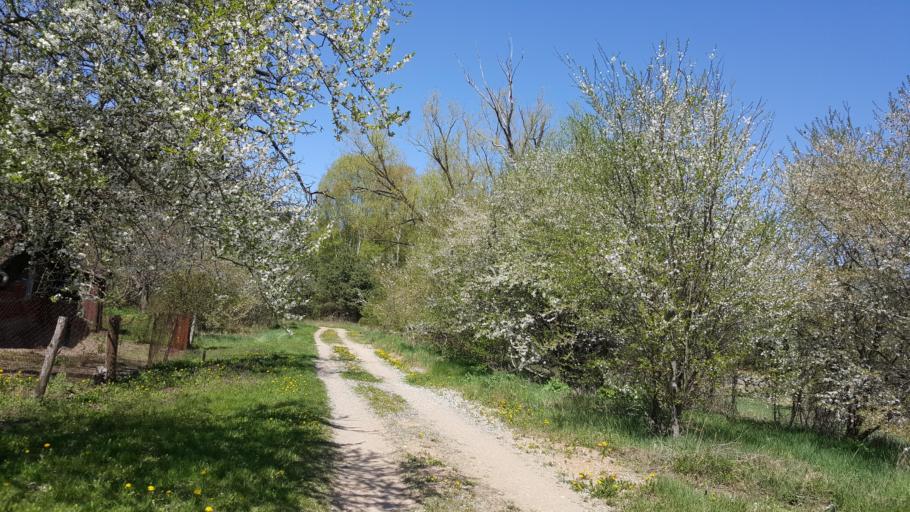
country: BY
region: Brest
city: Charnawchytsy
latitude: 52.3304
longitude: 23.6917
